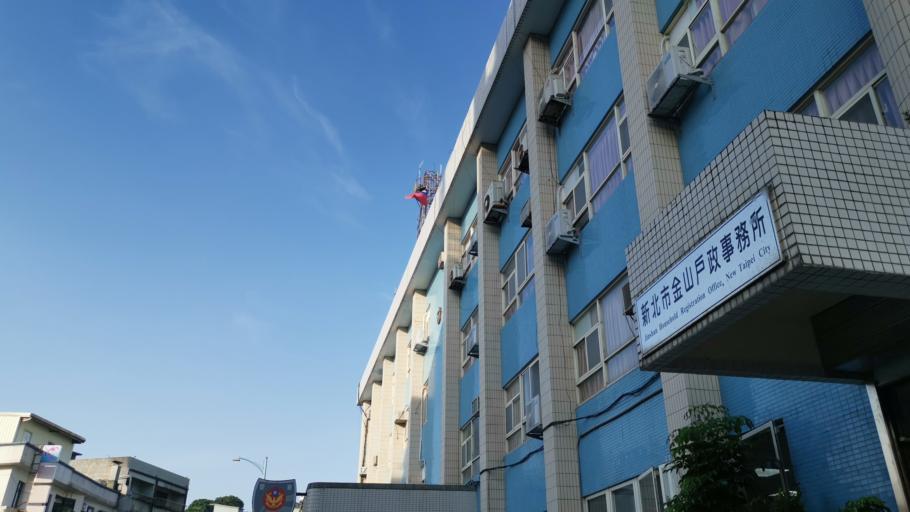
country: TW
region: Taiwan
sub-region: Keelung
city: Keelung
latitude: 25.2202
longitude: 121.6403
